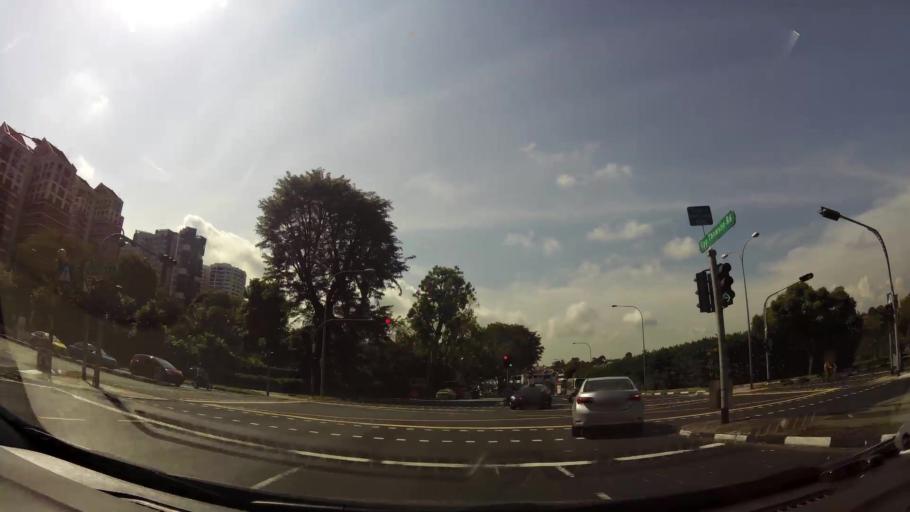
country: SG
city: Singapore
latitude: 1.3596
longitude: 103.8289
